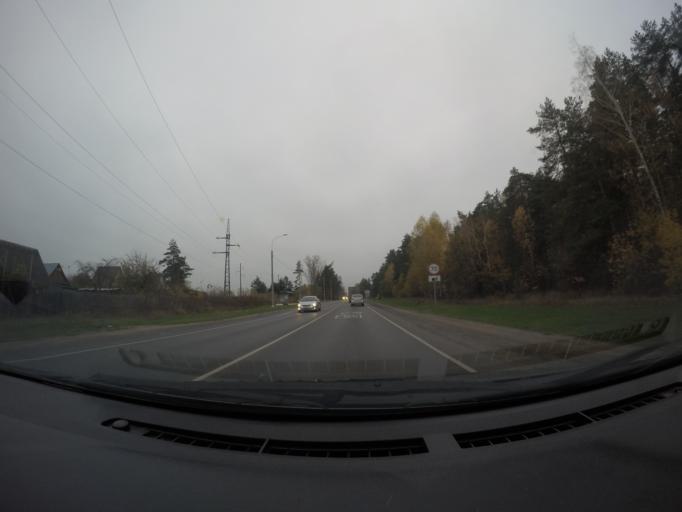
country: RU
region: Moskovskaya
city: Malyshevo
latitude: 55.4748
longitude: 38.3438
